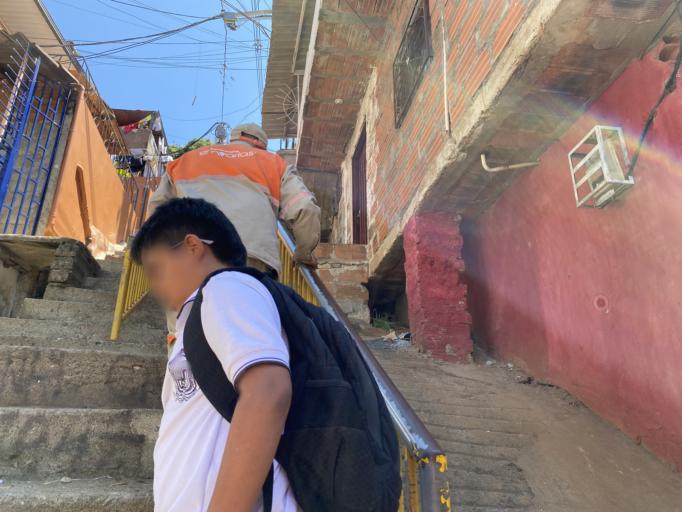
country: CO
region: Antioquia
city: Bello
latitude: 6.2953
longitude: -75.5515
